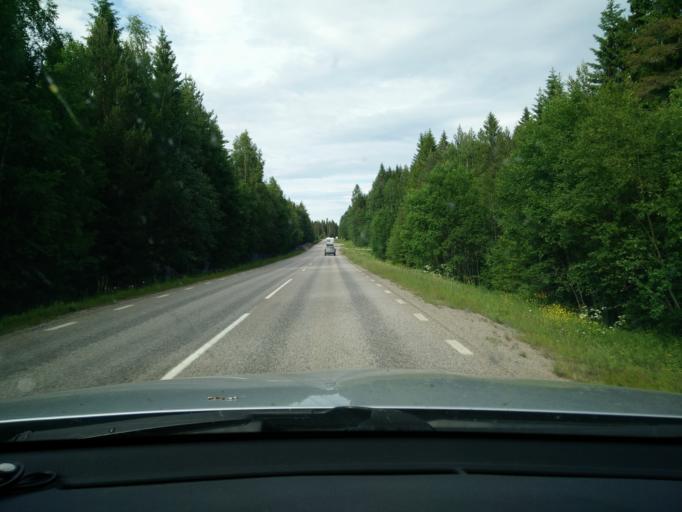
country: SE
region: Gaevleborg
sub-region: Nordanstigs Kommun
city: Bergsjoe
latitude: 61.9314
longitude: 17.0349
